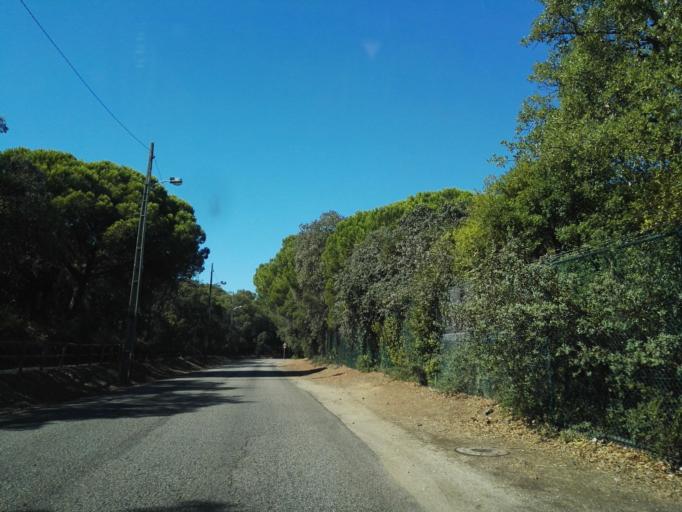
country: PT
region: Lisbon
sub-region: Odivelas
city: Pontinha
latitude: 38.7379
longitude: -9.1852
